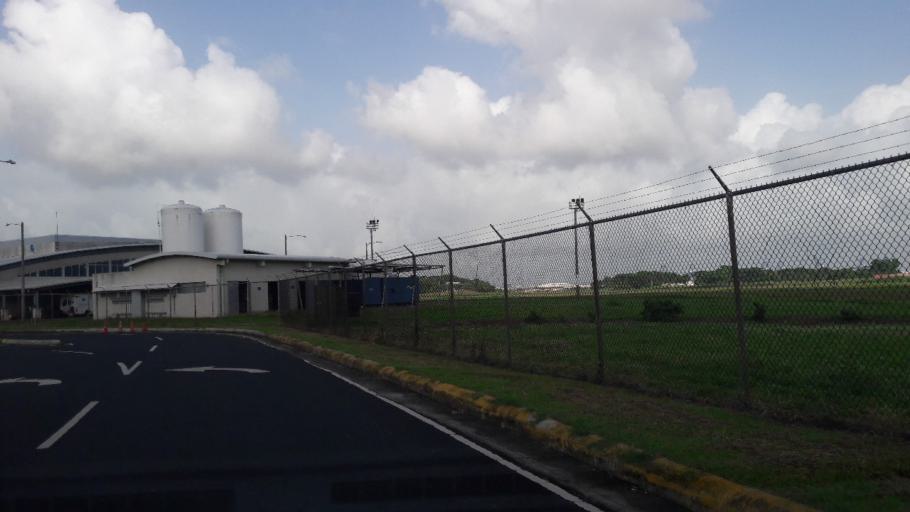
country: PA
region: Colon
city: Cativa
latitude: 9.3612
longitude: -79.8636
